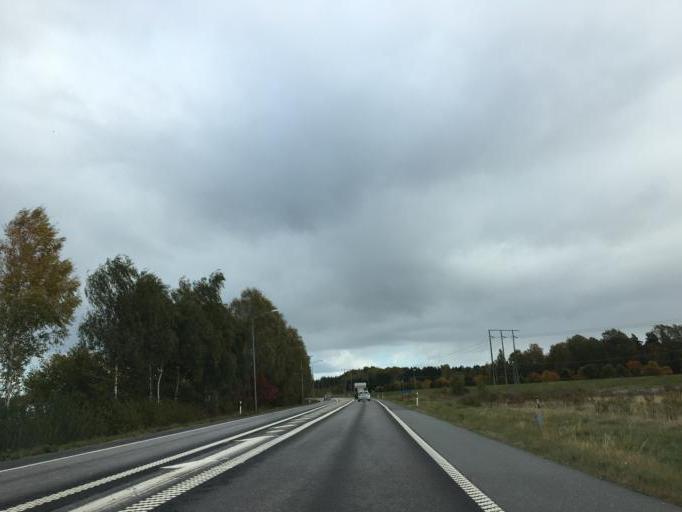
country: SE
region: Soedermanland
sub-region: Nykopings Kommun
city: Nykoping
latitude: 58.7665
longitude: 16.9722
